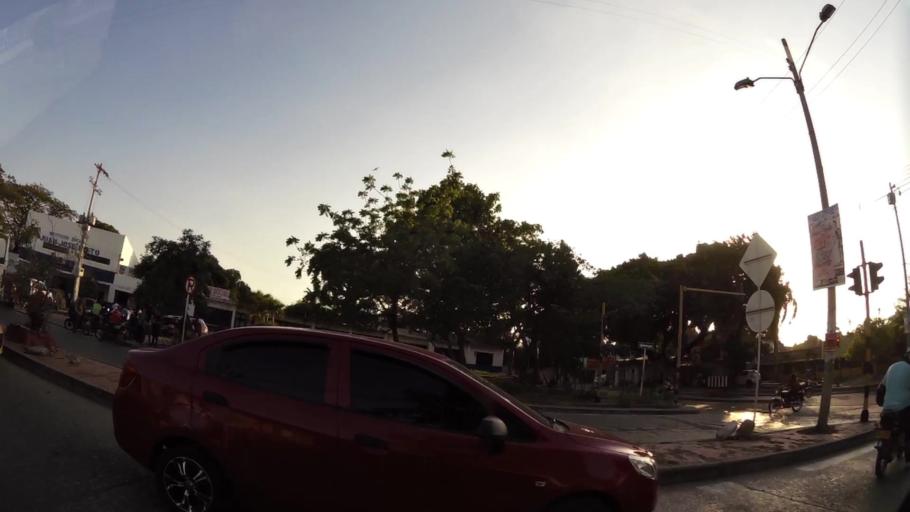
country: CO
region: Bolivar
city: Cartagena
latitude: 10.3867
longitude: -75.4818
